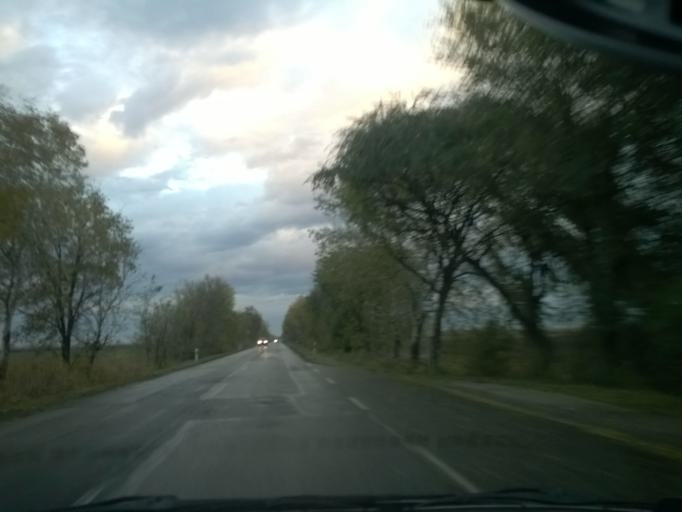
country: HU
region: Bacs-Kiskun
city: Szalkszentmarton
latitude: 46.9962
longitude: 19.0127
